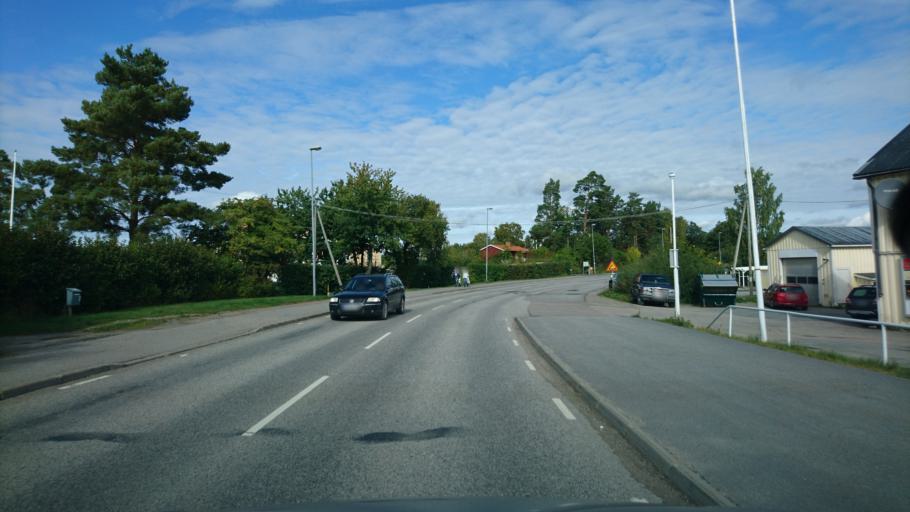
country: SE
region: Soedermanland
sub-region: Strangnas Kommun
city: Stallarholmen
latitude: 59.3626
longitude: 17.2047
